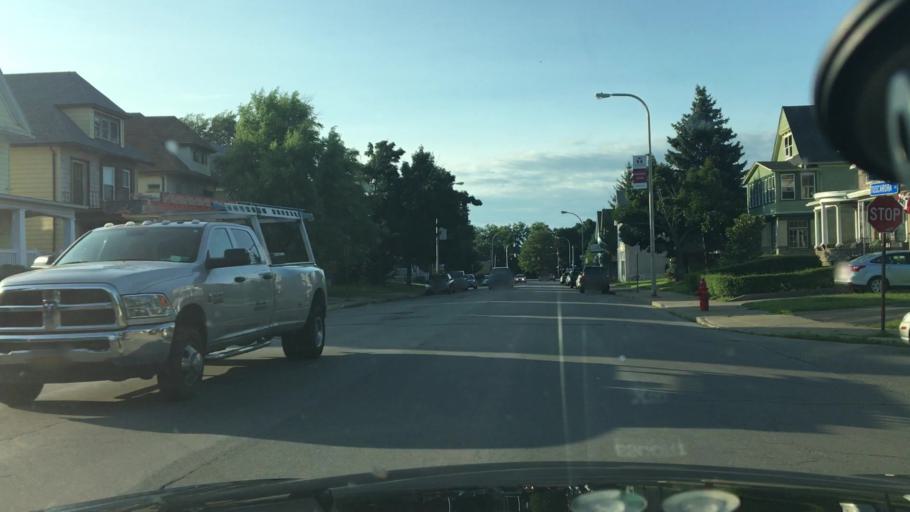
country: US
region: New York
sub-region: Erie County
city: West Seneca
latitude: 42.8444
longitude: -78.8095
